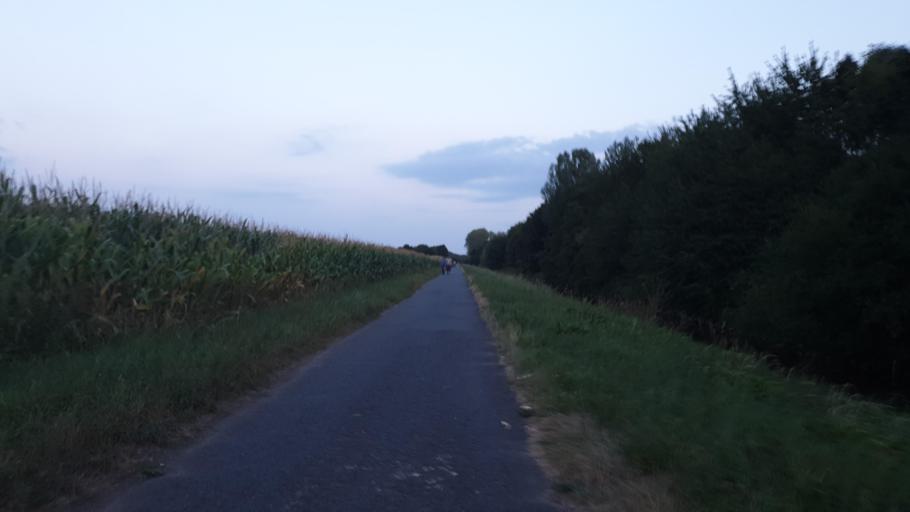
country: DE
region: North Rhine-Westphalia
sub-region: Regierungsbezirk Koln
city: Bergheim
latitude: 50.9382
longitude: 6.6565
